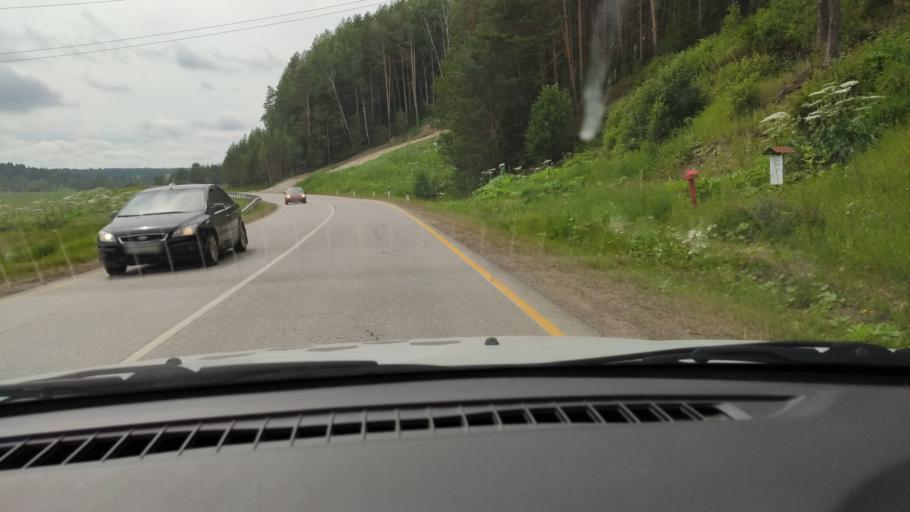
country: RU
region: Perm
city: Kukushtan
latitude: 57.4898
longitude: 56.6312
